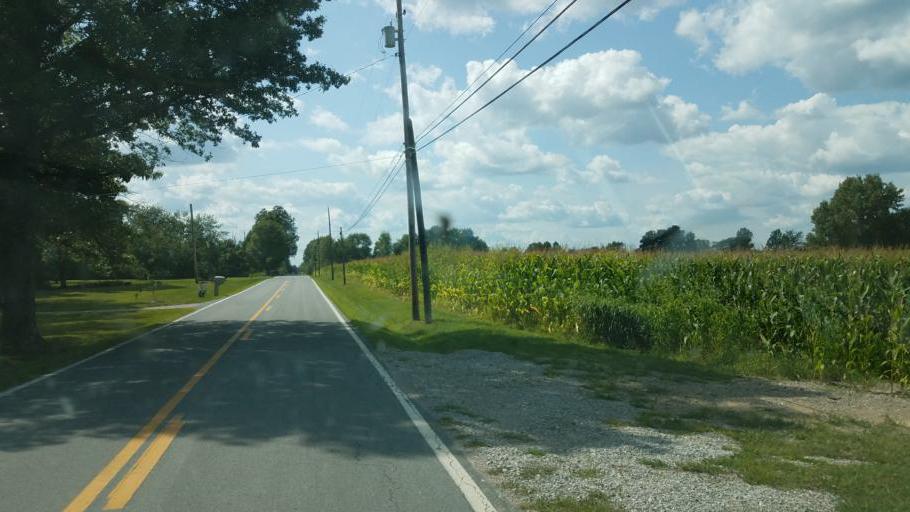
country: US
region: Ohio
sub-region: Delaware County
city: Lewis Center
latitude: 40.2261
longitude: -82.9986
